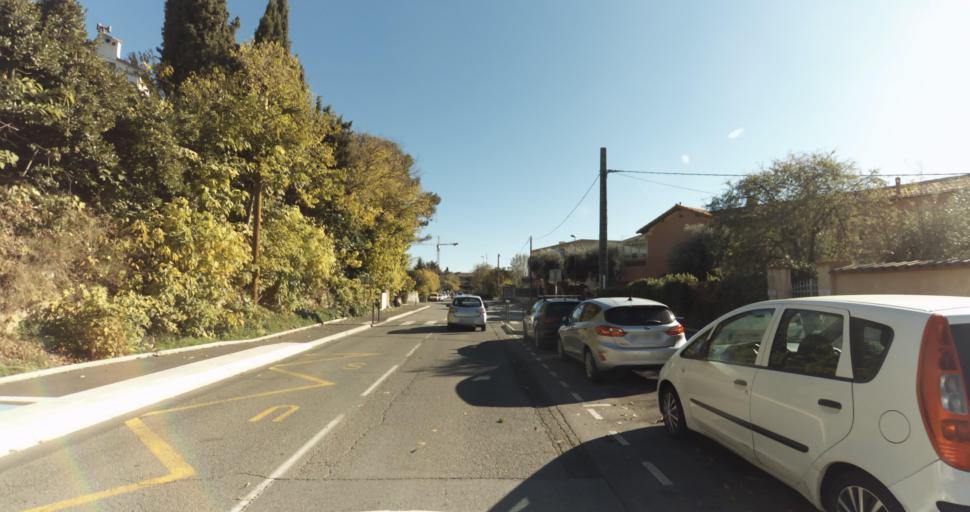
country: FR
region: Provence-Alpes-Cote d'Azur
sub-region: Departement des Alpes-Maritimes
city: Vence
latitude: 43.7247
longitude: 7.0996
